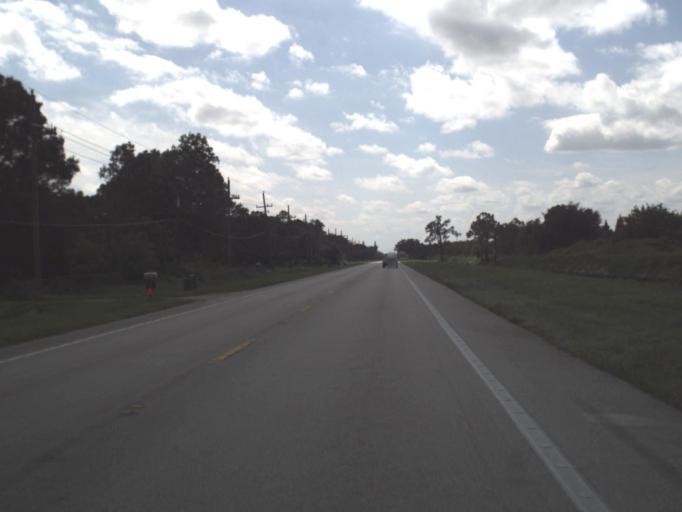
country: US
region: Florida
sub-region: Hendry County
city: LaBelle
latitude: 26.6898
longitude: -81.4369
